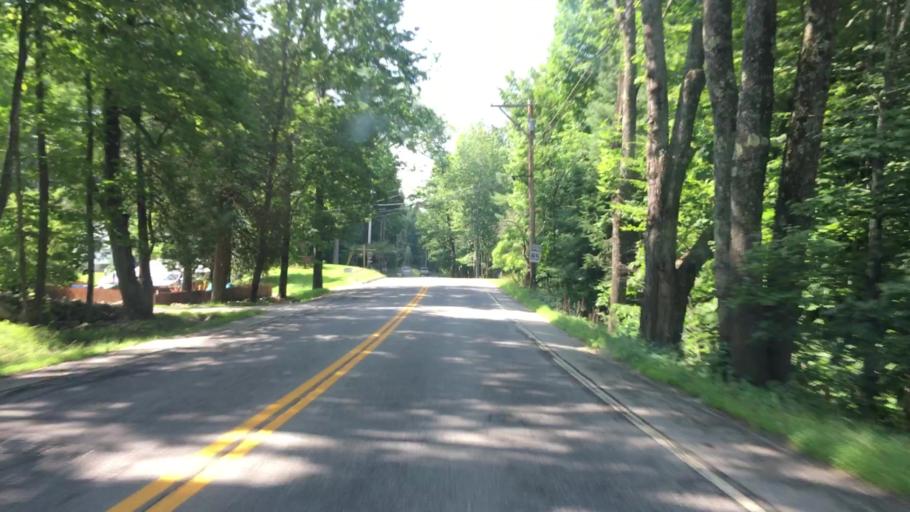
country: US
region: Maine
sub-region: Cumberland County
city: Raymond
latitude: 43.9109
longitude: -70.4397
